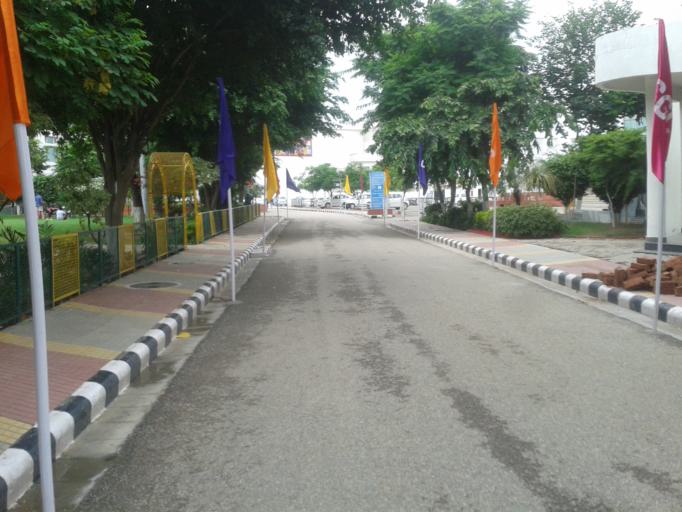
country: IN
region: Punjab
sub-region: Ajitgarh
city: Mohali
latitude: 30.6870
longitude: 76.6648
